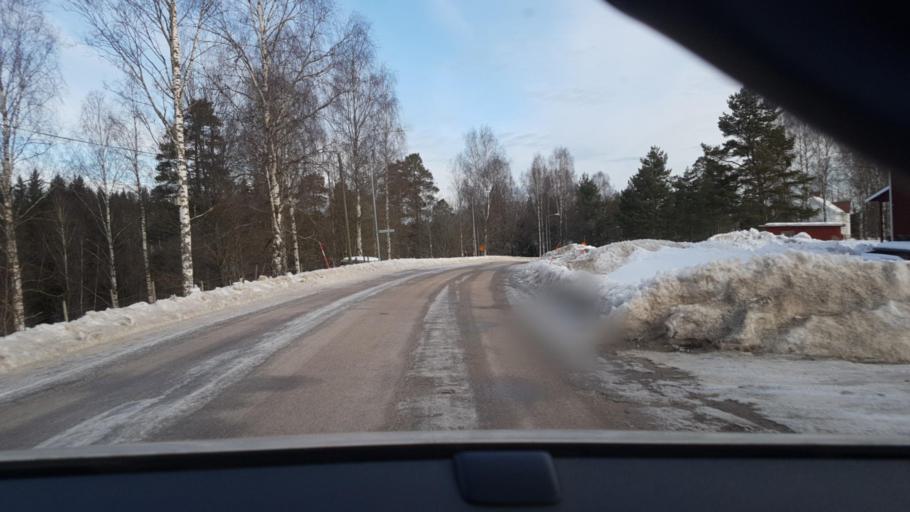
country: SE
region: Vaermland
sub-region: Eda Kommun
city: Amotfors
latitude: 59.7085
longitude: 12.1467
